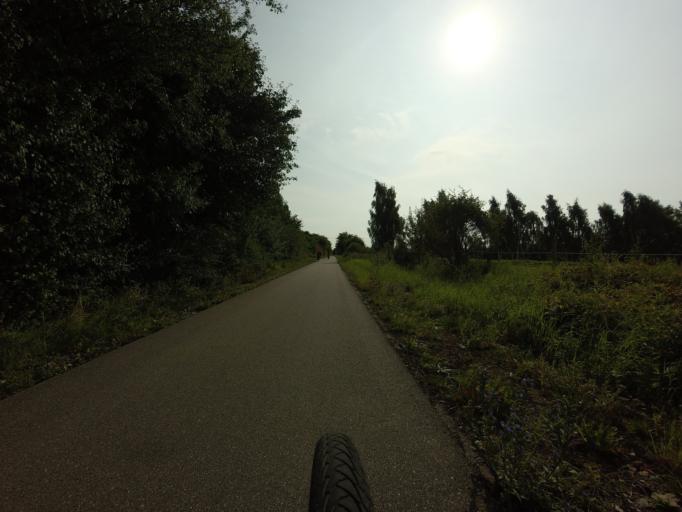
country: DK
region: Zealand
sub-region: Naestved Kommune
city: Fuglebjerg
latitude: 55.2633
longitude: 11.5423
